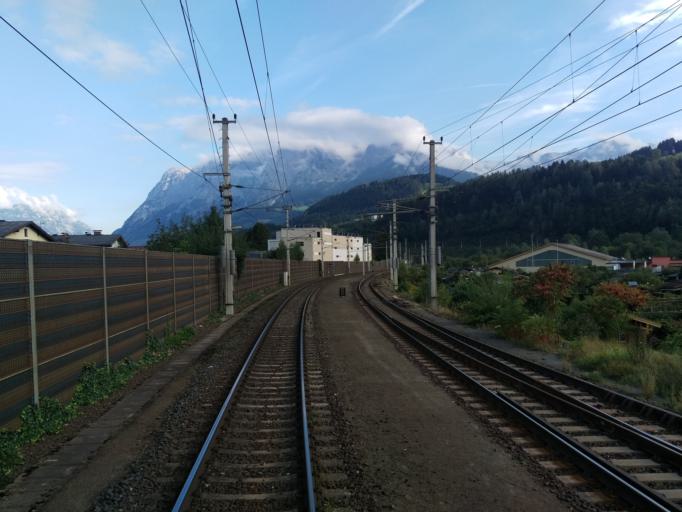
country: AT
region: Salzburg
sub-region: Politischer Bezirk Sankt Johann im Pongau
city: Bischofshofen
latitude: 47.4230
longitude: 13.2196
